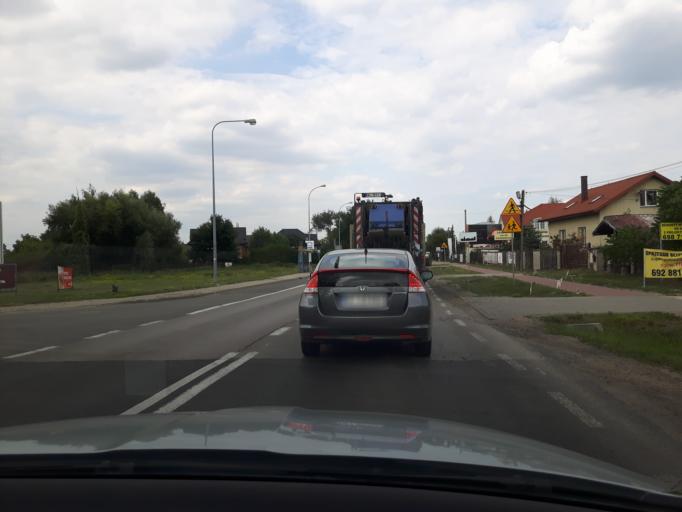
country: PL
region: Masovian Voivodeship
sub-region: Powiat legionowski
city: Stanislawow Pierwszy
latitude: 52.3645
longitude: 21.0282
